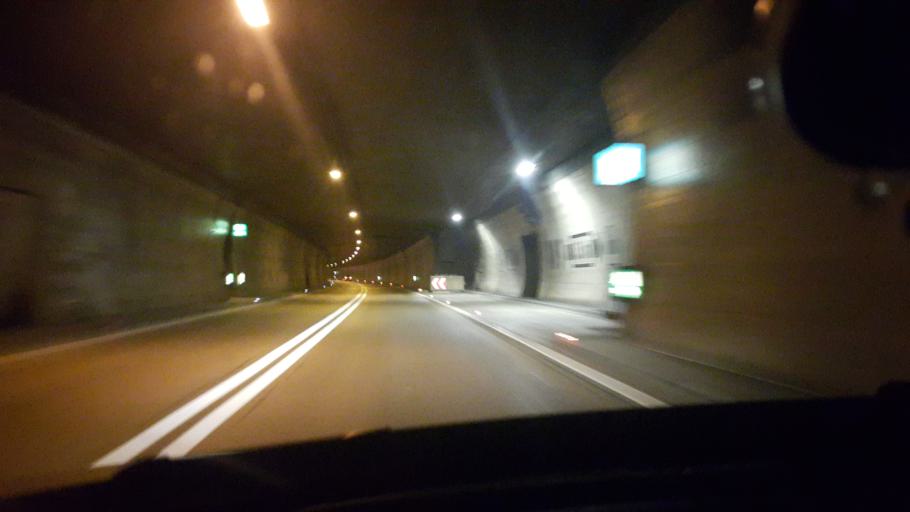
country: AT
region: Styria
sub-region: Graz Stadt
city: Wetzelsdorf
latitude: 47.0449
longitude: 15.4027
